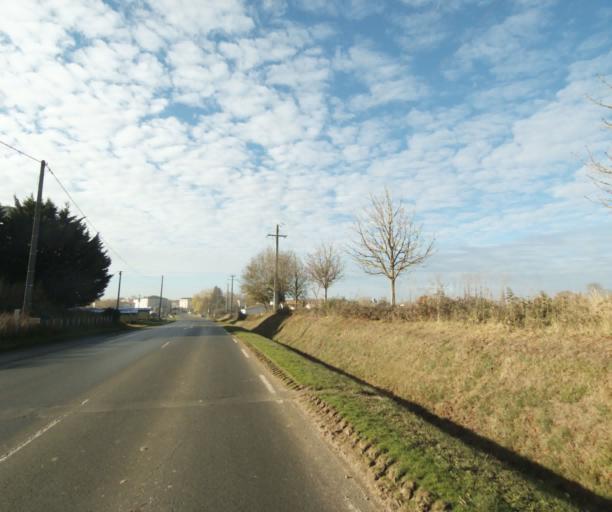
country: FR
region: Poitou-Charentes
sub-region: Departement de la Charente-Maritime
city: Corme-Royal
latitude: 45.7019
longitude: -0.7774
